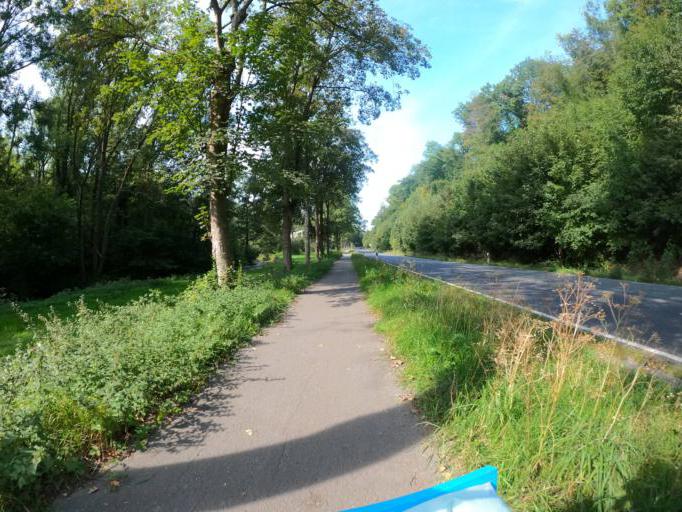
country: DE
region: North Rhine-Westphalia
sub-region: Regierungsbezirk Dusseldorf
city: Erkrath
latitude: 51.2269
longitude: 6.9361
